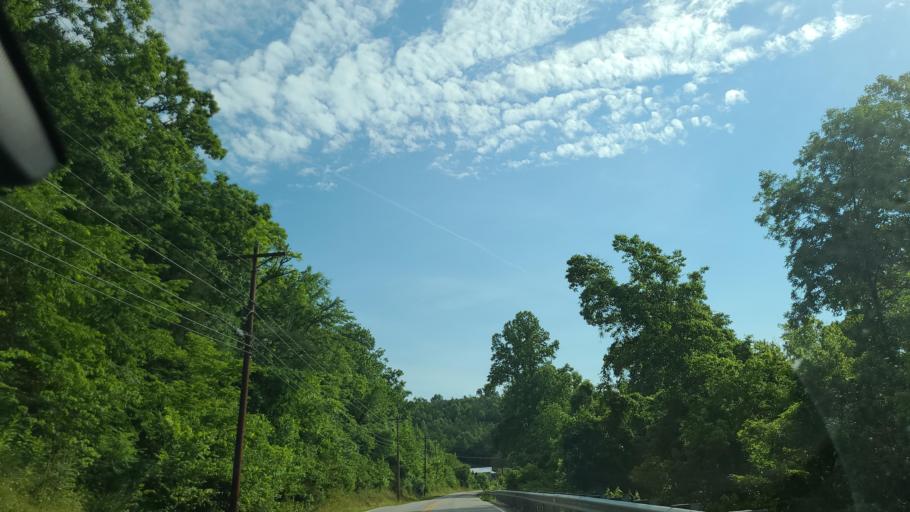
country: US
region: Kentucky
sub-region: Whitley County
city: Williamsburg
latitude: 36.7492
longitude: -84.0336
